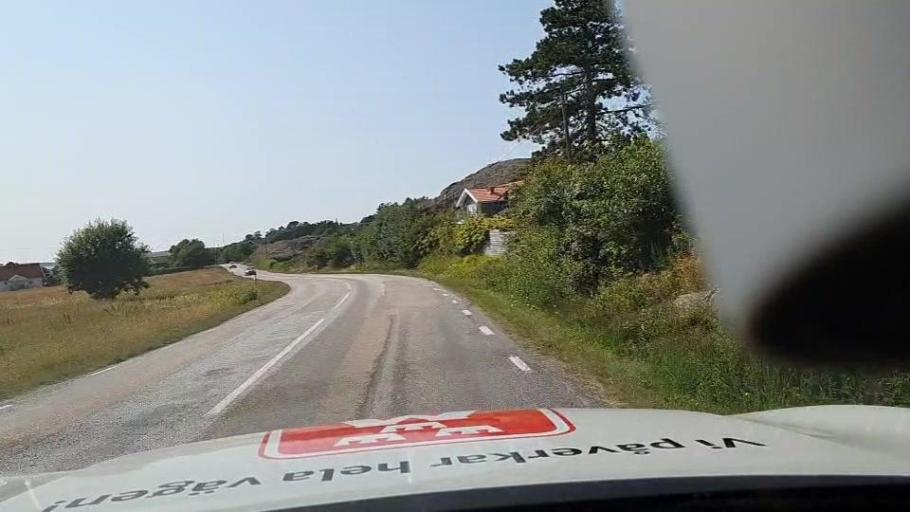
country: SE
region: Vaestra Goetaland
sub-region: Tjorns Kommun
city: Skaerhamn
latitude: 58.1068
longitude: 11.4810
